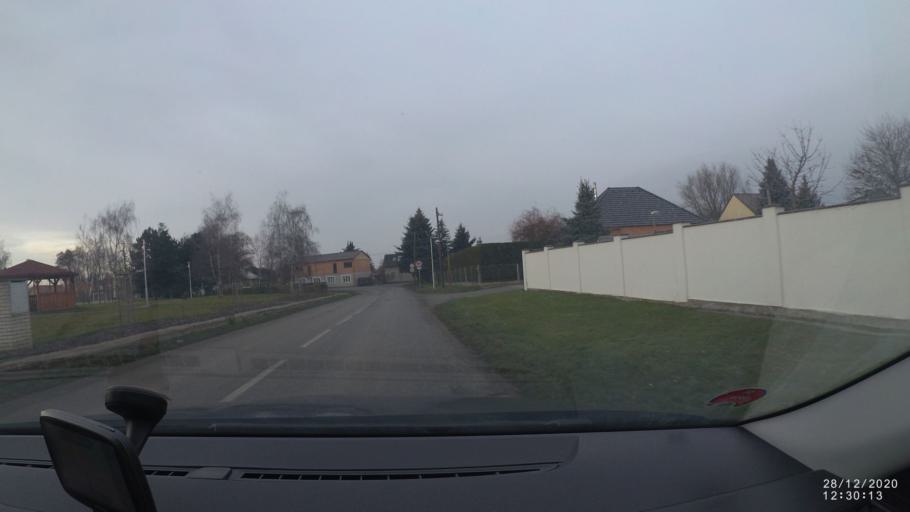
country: CZ
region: Central Bohemia
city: Kostelec nad Labem
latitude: 50.2000
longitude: 14.6005
